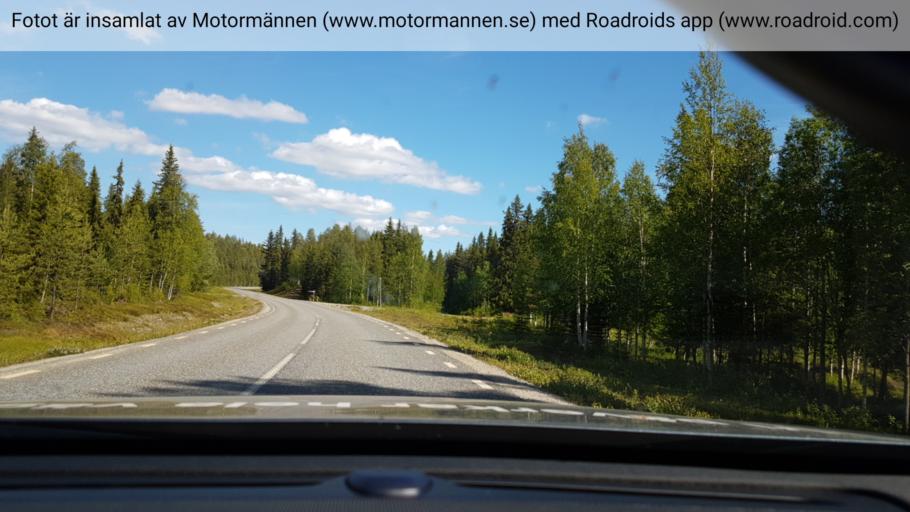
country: SE
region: Vaesterbotten
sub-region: Lycksele Kommun
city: Lycksele
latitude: 64.6033
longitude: 18.5139
